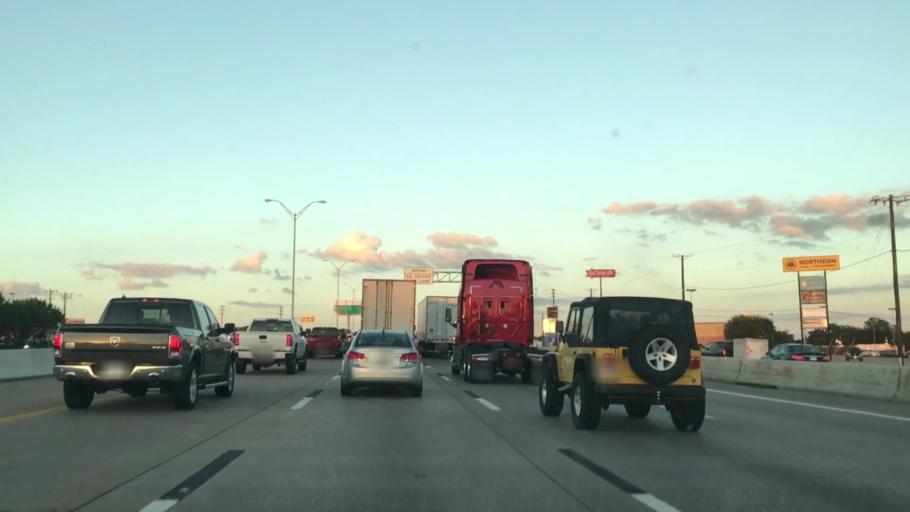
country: US
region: Texas
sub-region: Dallas County
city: Sunnyvale
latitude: 32.8384
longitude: -96.5994
